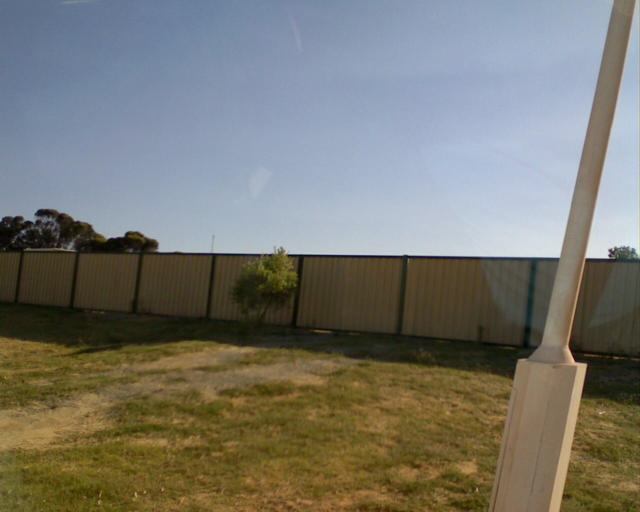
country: AU
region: Western Australia
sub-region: Dandaragan
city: Jurien Bay
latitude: -30.0666
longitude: 114.9724
